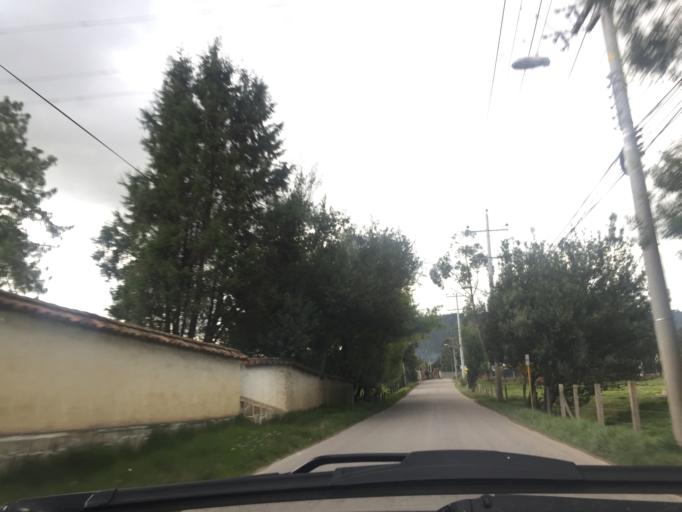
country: CO
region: Cundinamarca
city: Sopo
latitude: 4.9390
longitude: -73.9489
